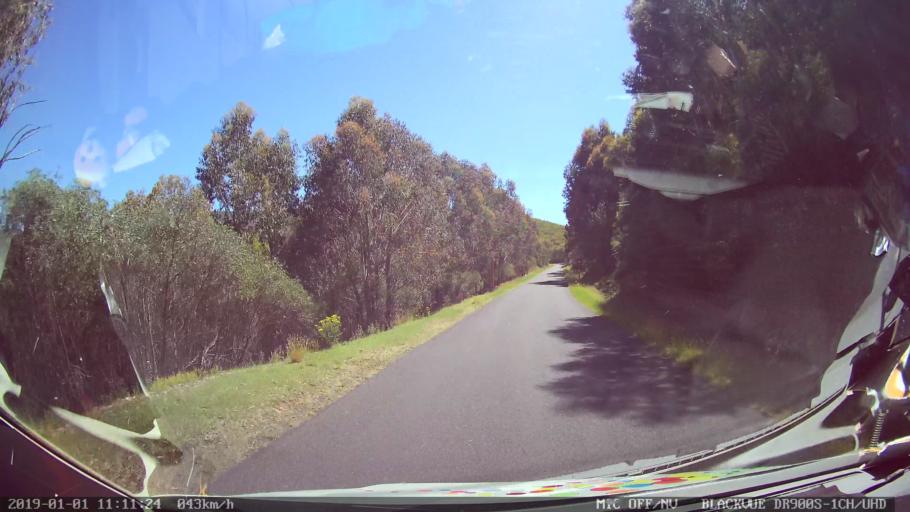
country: AU
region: New South Wales
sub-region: Snowy River
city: Jindabyne
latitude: -35.9623
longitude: 148.4000
